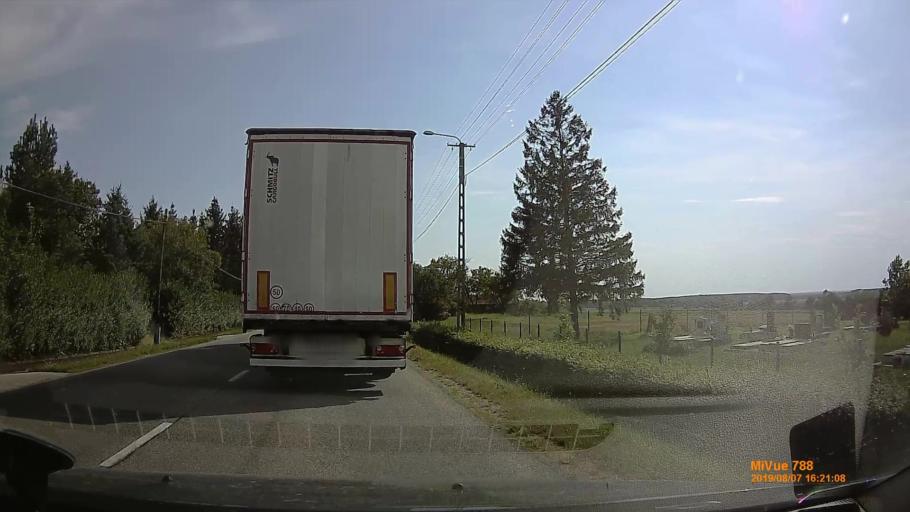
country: HU
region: Zala
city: Zalalovo
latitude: 46.7653
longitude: 16.5656
